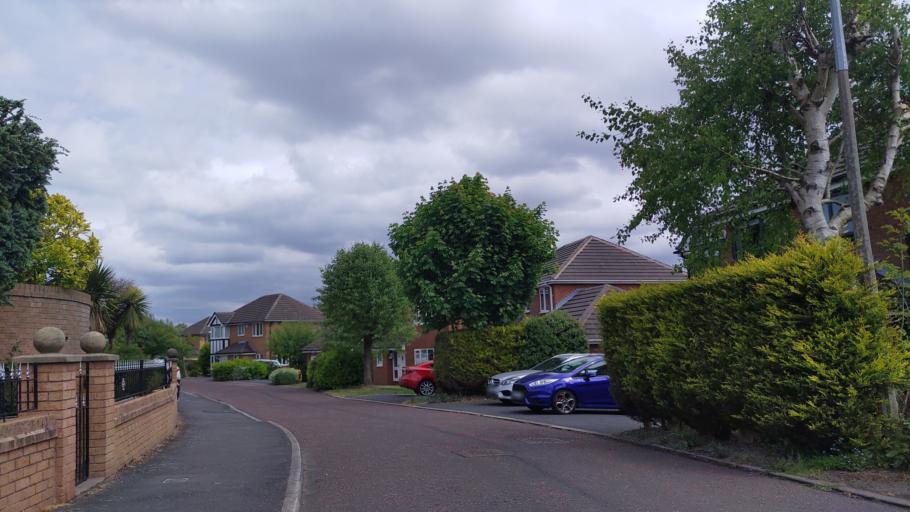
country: GB
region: England
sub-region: Lancashire
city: Chorley
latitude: 53.6690
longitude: -2.6138
